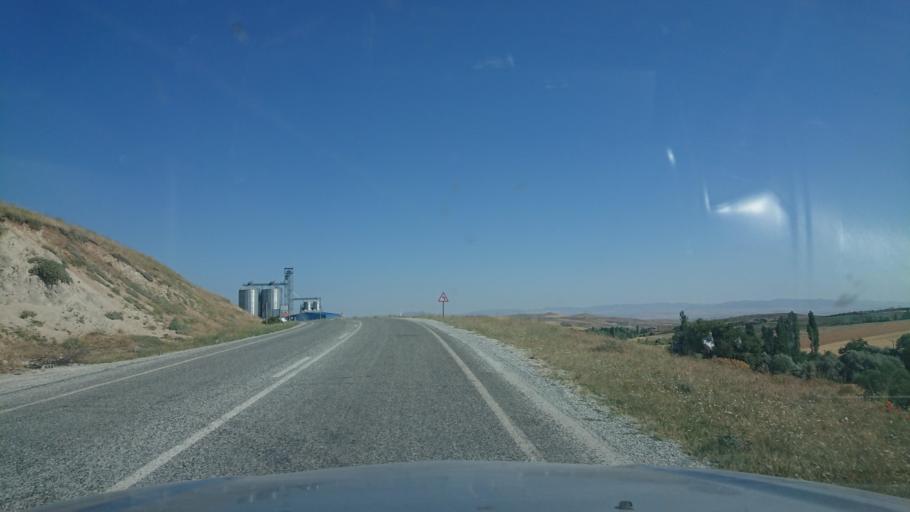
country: TR
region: Aksaray
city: Agacoren
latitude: 38.8665
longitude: 33.8953
